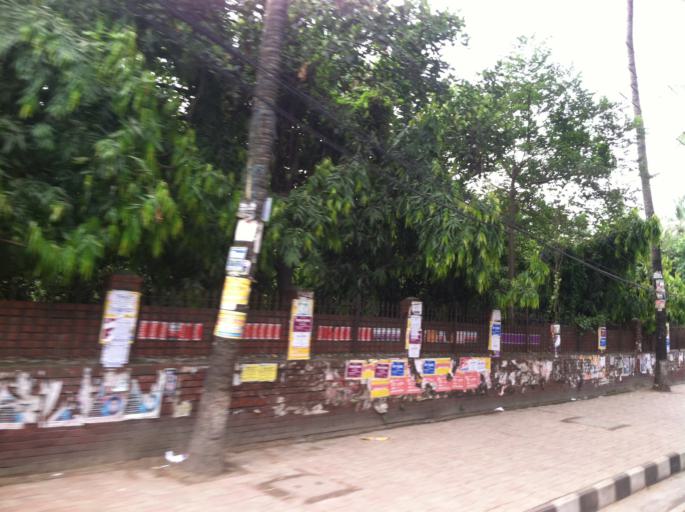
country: BD
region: Dhaka
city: Azimpur
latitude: 23.7592
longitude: 90.3871
